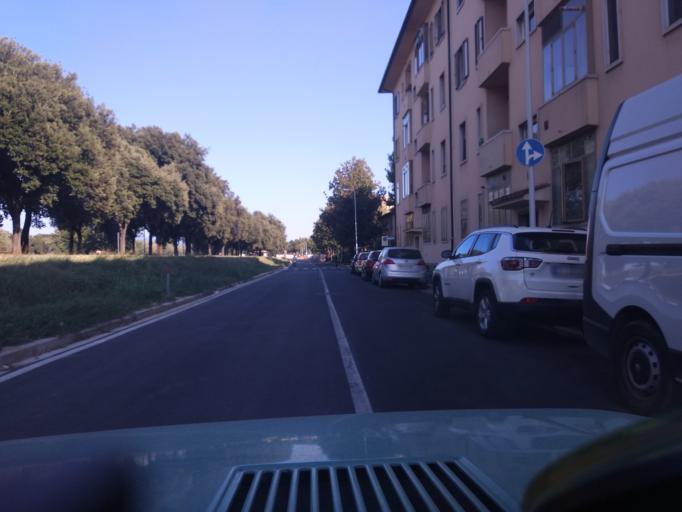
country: IT
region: Tuscany
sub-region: Province of Florence
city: Florence
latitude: 43.7804
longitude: 11.2152
